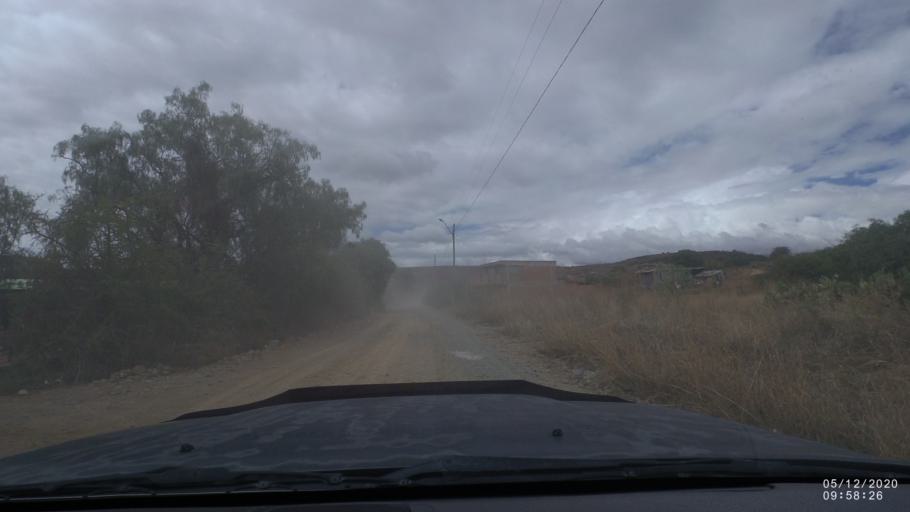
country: BO
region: Cochabamba
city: Sipe Sipe
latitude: -17.4293
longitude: -66.2916
